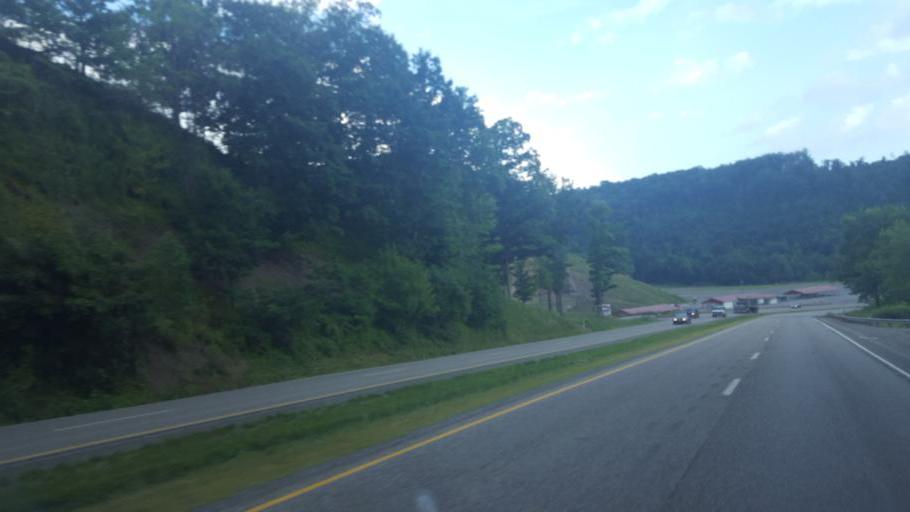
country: US
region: Virginia
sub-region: Wise County
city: Wise
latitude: 37.0118
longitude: -82.5905
